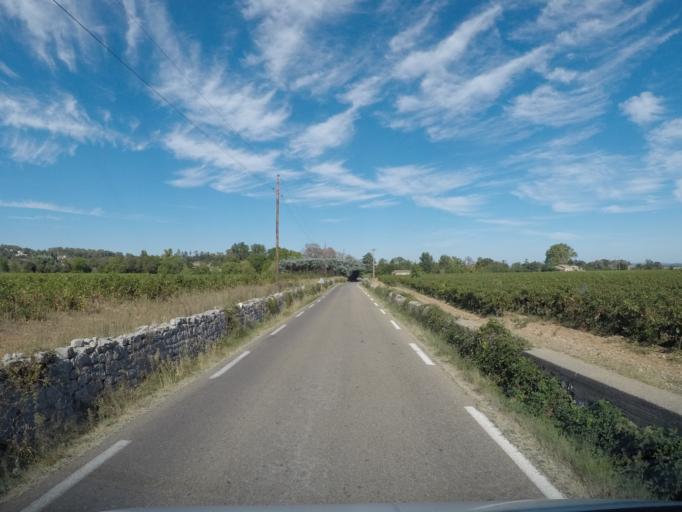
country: FR
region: Languedoc-Roussillon
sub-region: Departement du Gard
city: Boisset-et-Gaujac
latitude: 44.0164
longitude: 3.9923
